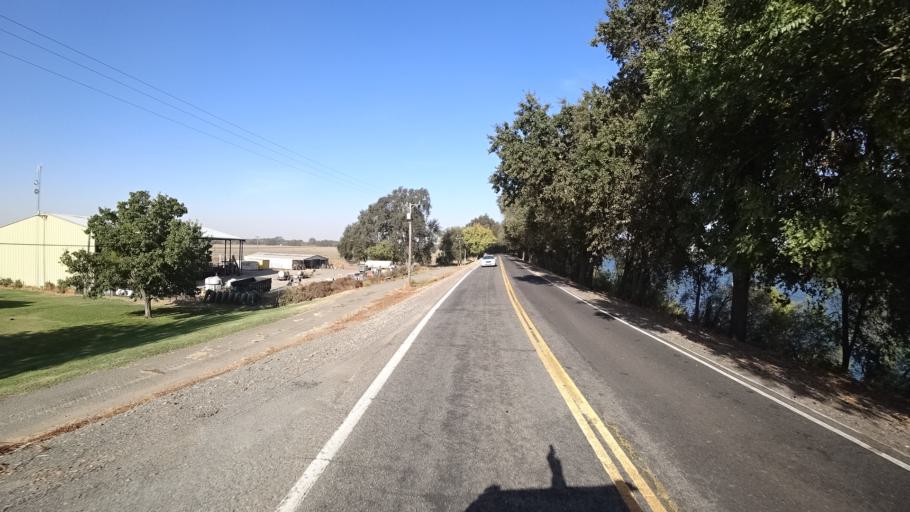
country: US
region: California
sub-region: Sacramento County
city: Parkway
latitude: 38.4750
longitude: -121.5427
